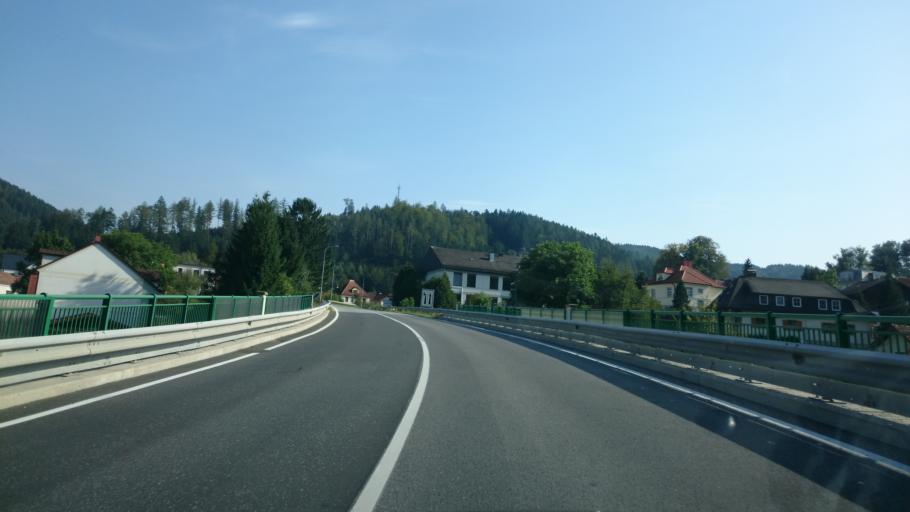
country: AT
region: Lower Austria
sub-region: Politischer Bezirk Neunkirchen
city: Thomasberg
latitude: 47.5537
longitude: 16.0860
